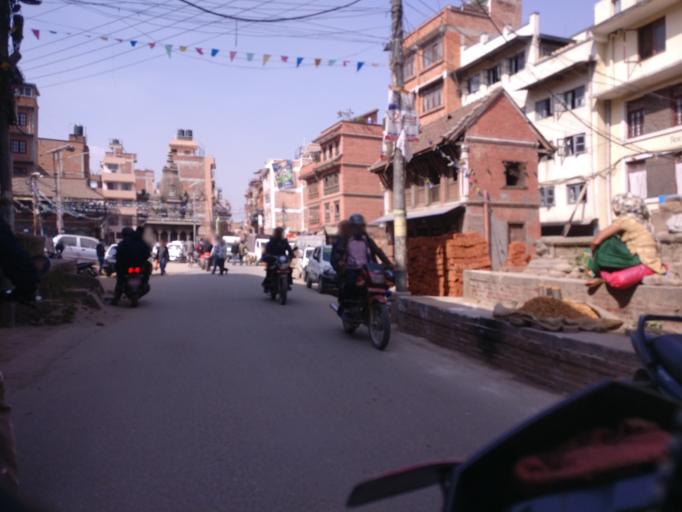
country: NP
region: Central Region
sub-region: Bagmati Zone
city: Patan
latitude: 27.6694
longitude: 85.3285
